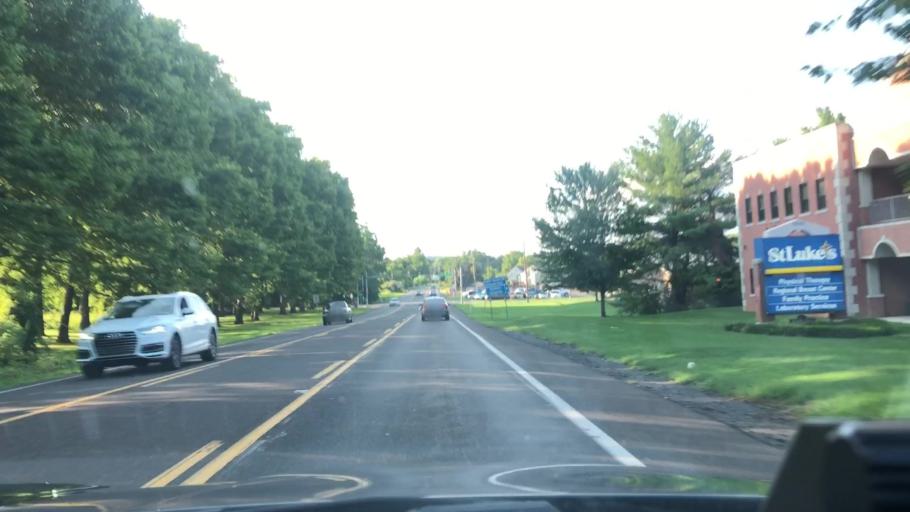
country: US
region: Pennsylvania
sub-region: Lehigh County
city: Coopersburg
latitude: 40.5346
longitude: -75.3953
